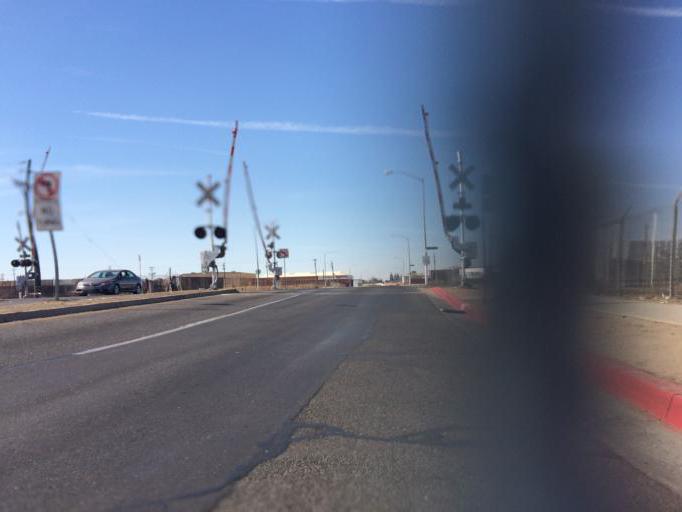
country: US
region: California
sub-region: Fresno County
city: Fresno
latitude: 36.7287
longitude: -119.7722
